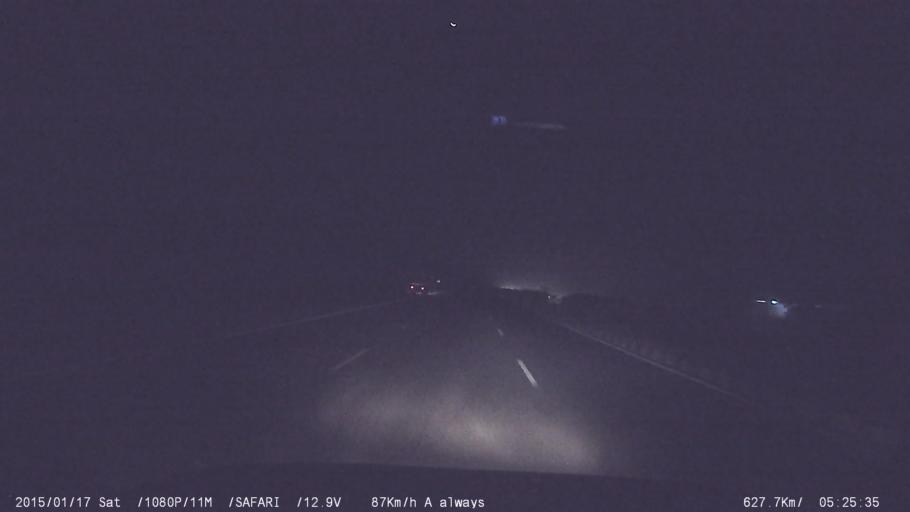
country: IN
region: Tamil Nadu
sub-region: Vellore
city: Arcot
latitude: 12.9421
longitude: 79.2352
